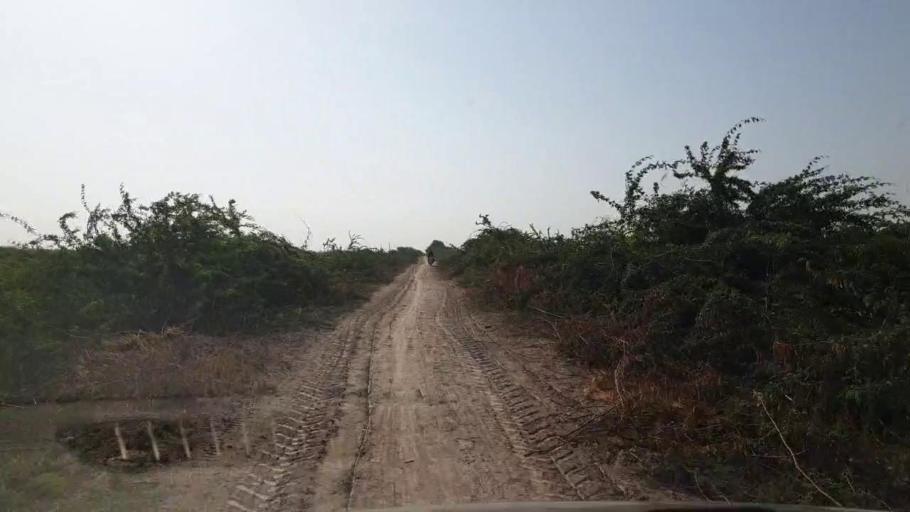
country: PK
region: Sindh
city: Kadhan
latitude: 24.5905
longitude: 69.0767
